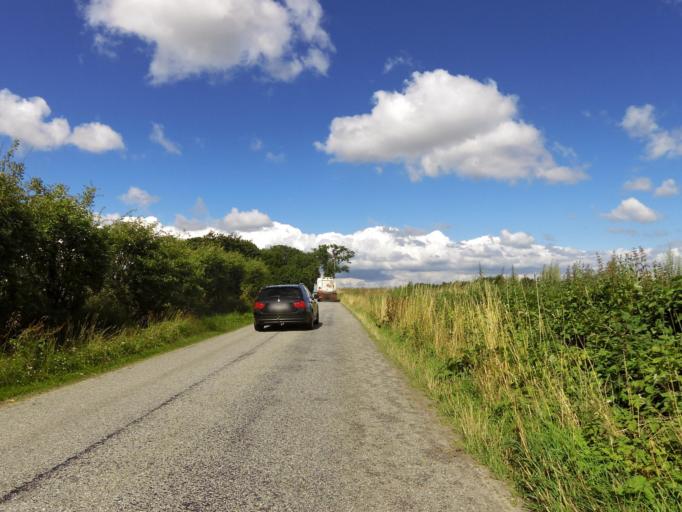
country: DK
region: South Denmark
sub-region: Haderslev Kommune
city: Gram
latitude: 55.2781
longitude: 9.0082
